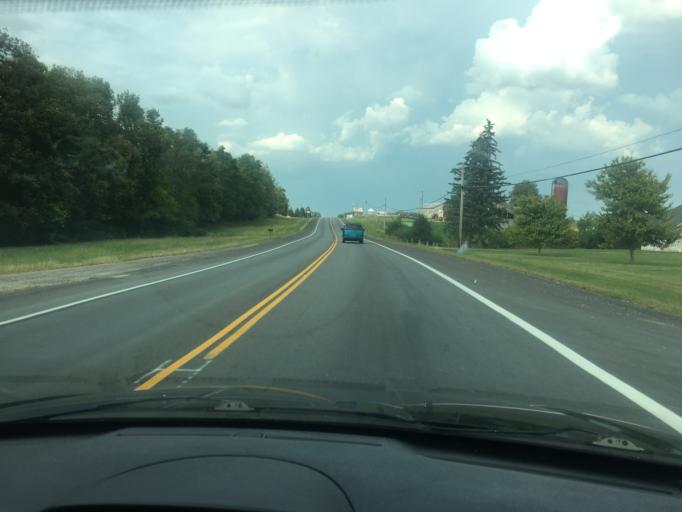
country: US
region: Ohio
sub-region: Champaign County
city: Urbana
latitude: 40.0760
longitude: -83.7654
